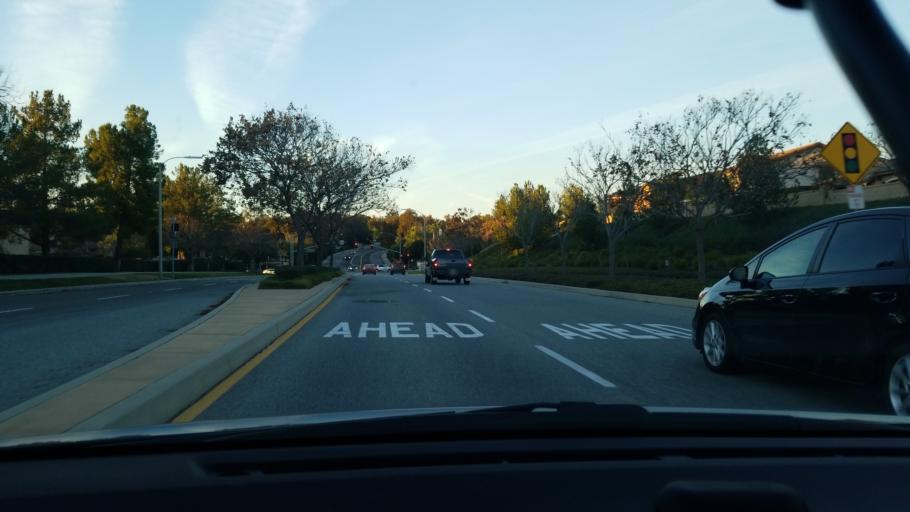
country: US
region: California
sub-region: Riverside County
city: Temecula
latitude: 33.5048
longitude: -117.0955
